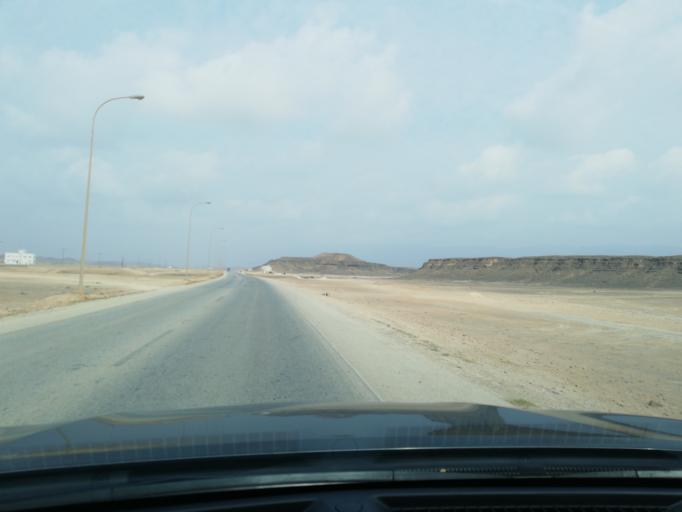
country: OM
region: Zufar
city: Salalah
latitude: 16.9511
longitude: 53.9324
